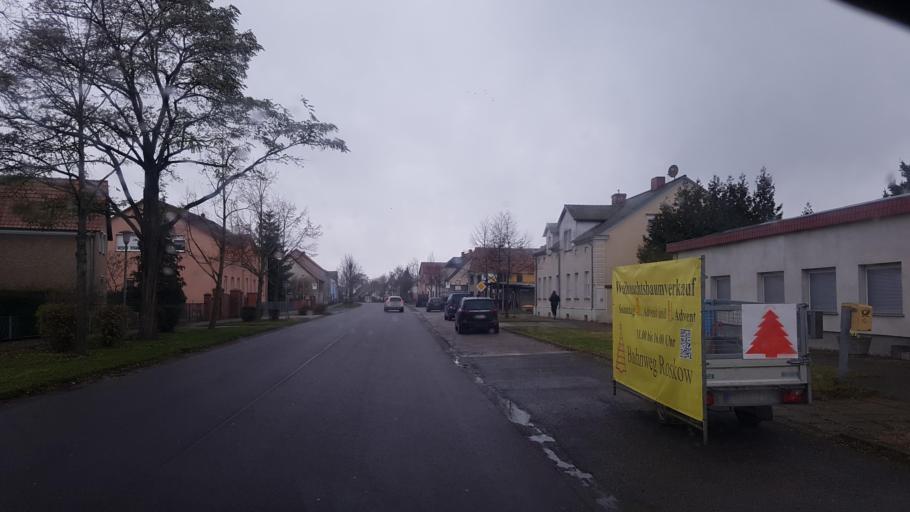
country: DE
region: Brandenburg
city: Roskow
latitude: 52.4627
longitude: 12.6752
